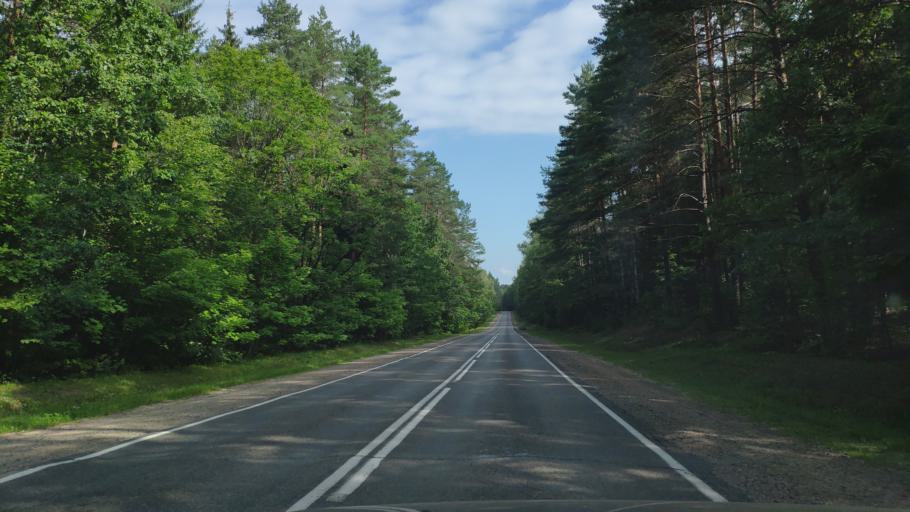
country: BY
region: Minsk
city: Novosel'ye
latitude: 53.9457
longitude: 27.2452
